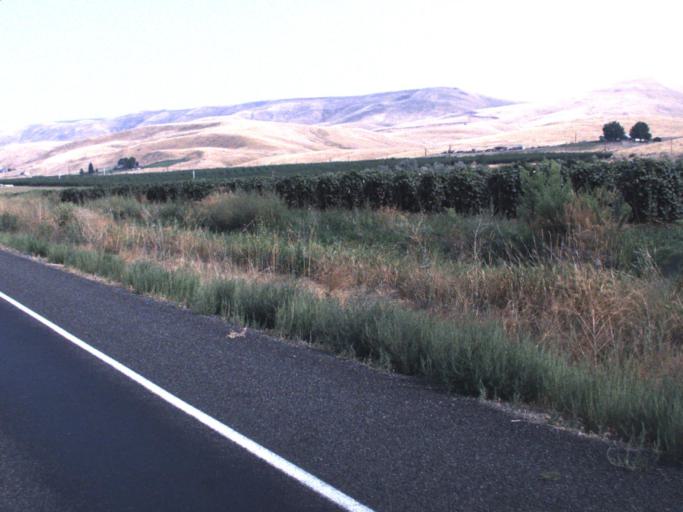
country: US
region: Washington
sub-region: Yakima County
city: Grandview
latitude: 46.1872
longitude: -119.8720
